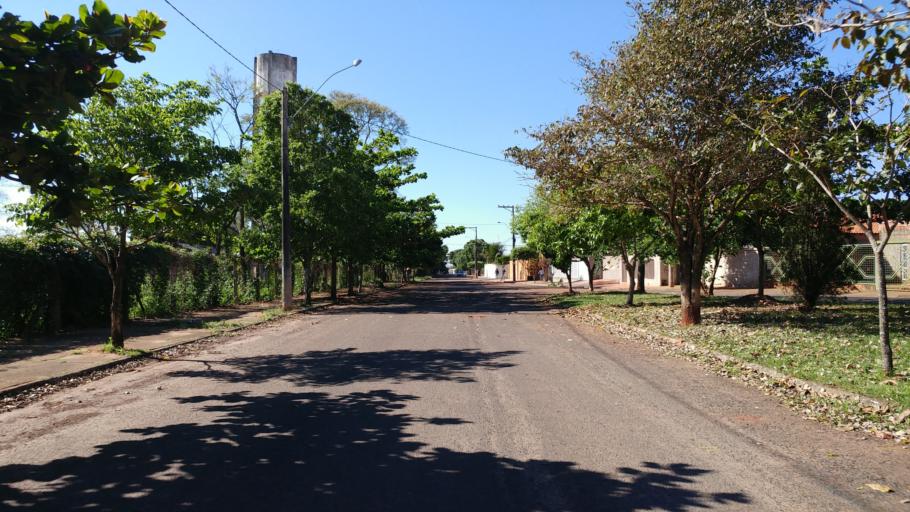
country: BR
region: Sao Paulo
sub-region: Paraguacu Paulista
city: Paraguacu Paulista
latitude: -22.4045
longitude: -50.5774
